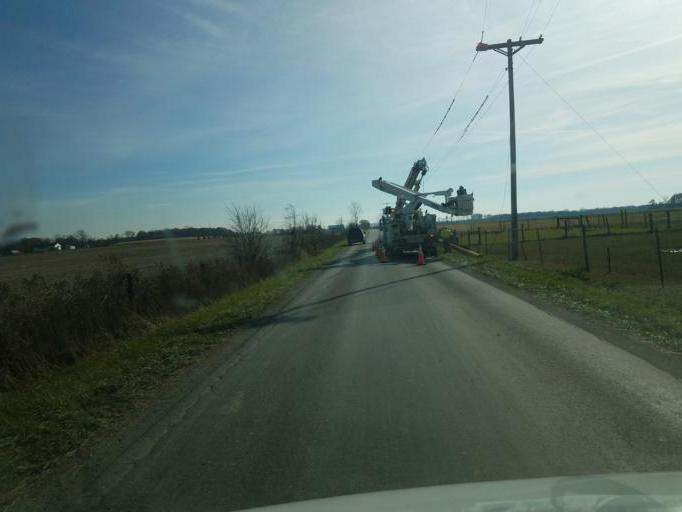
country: US
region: Ohio
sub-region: Hardin County
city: Kenton
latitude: 40.5756
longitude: -83.4535
